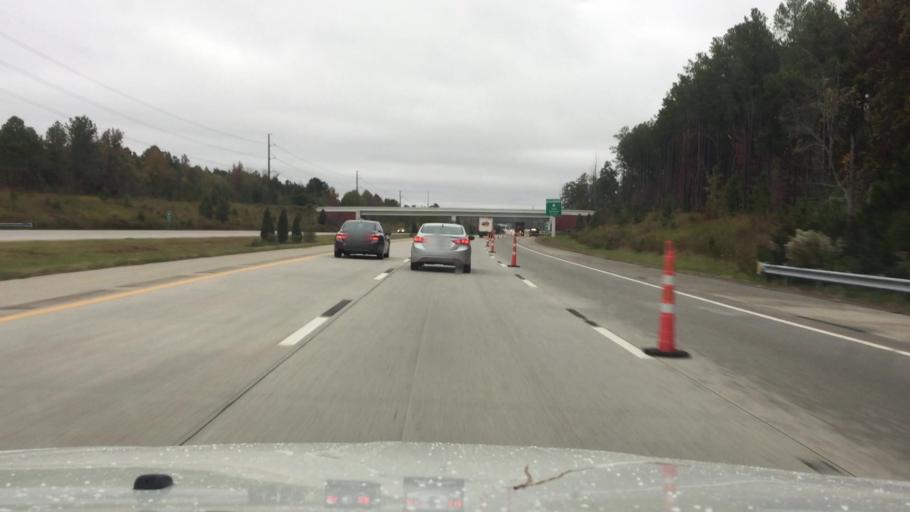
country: US
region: North Carolina
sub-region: Wake County
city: Green Level
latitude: 35.8066
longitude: -78.8920
